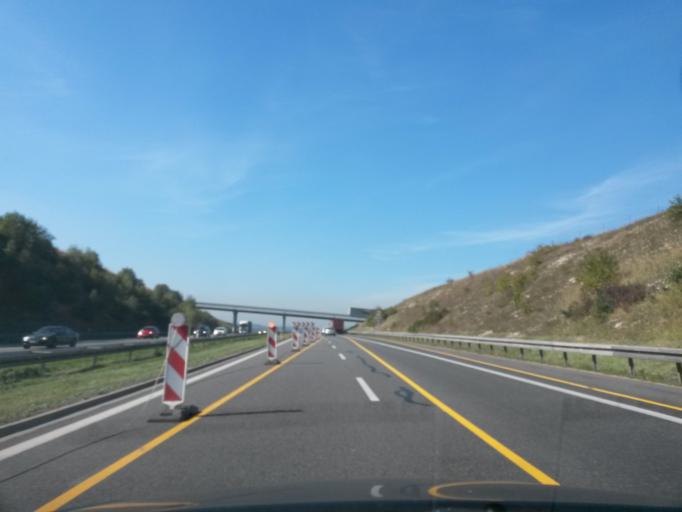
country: PL
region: Lesser Poland Voivodeship
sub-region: Powiat chrzanowski
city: Grojec
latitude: 50.0985
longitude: 19.5573
